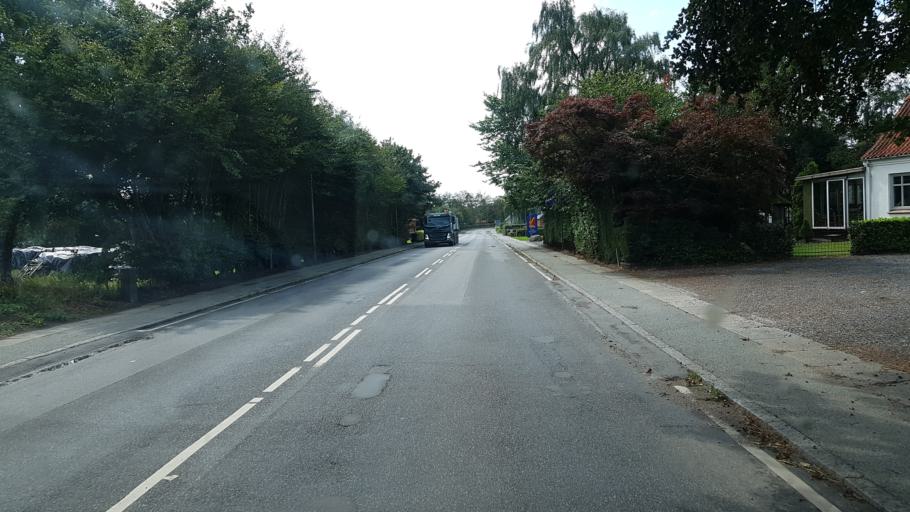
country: DK
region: South Denmark
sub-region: Vejen Kommune
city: Vejen
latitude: 55.5721
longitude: 9.1489
